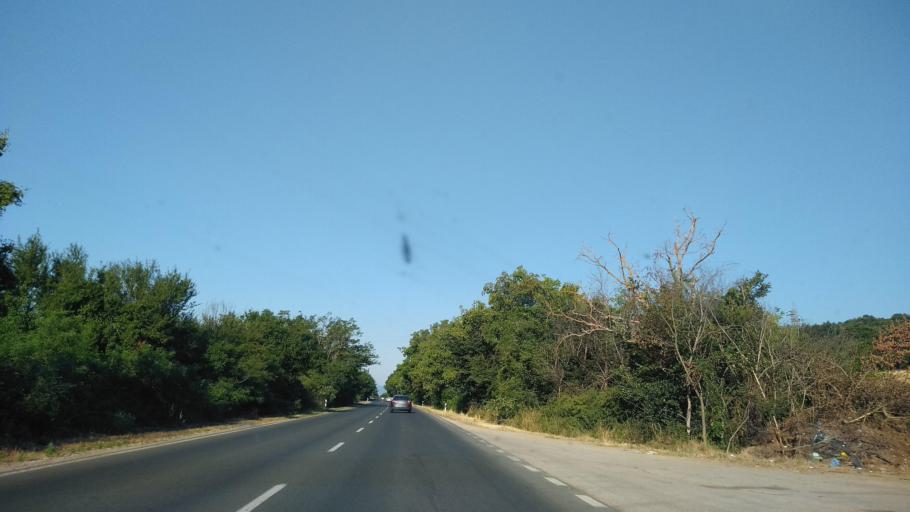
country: BG
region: Gabrovo
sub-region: Obshtina Sevlievo
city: Sevlievo
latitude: 43.0467
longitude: 25.2351
